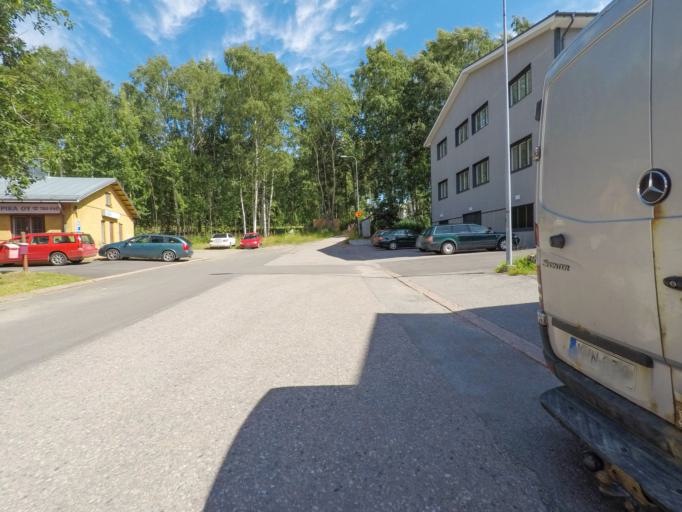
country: FI
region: Uusimaa
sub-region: Helsinki
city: Vantaa
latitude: 60.2065
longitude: 25.0558
